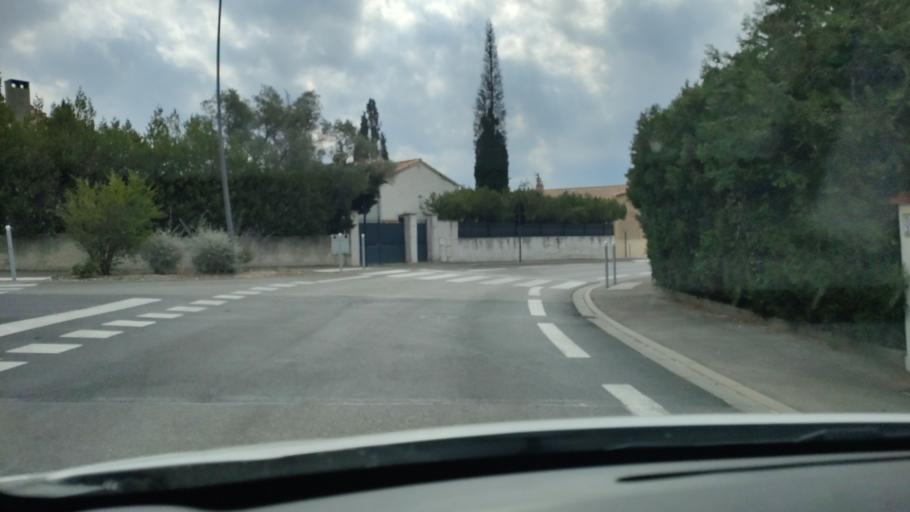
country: FR
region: Languedoc-Roussillon
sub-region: Departement du Gard
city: Les Angles
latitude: 43.9643
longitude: 4.7704
